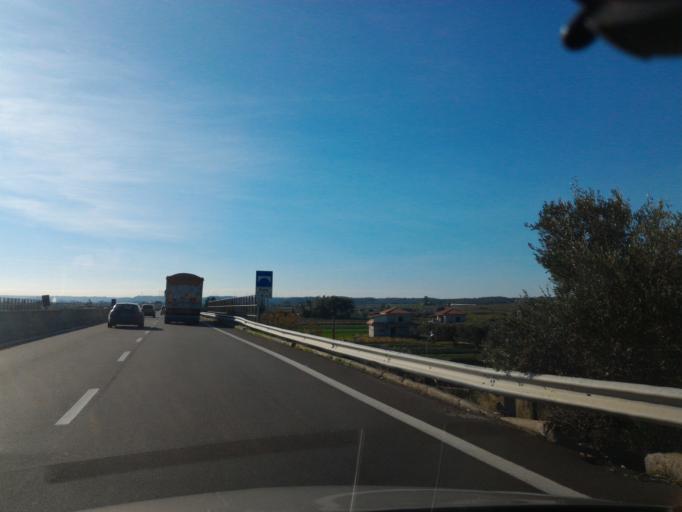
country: IT
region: Calabria
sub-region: Provincia di Crotone
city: Crotone
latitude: 39.1619
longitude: 17.0981
